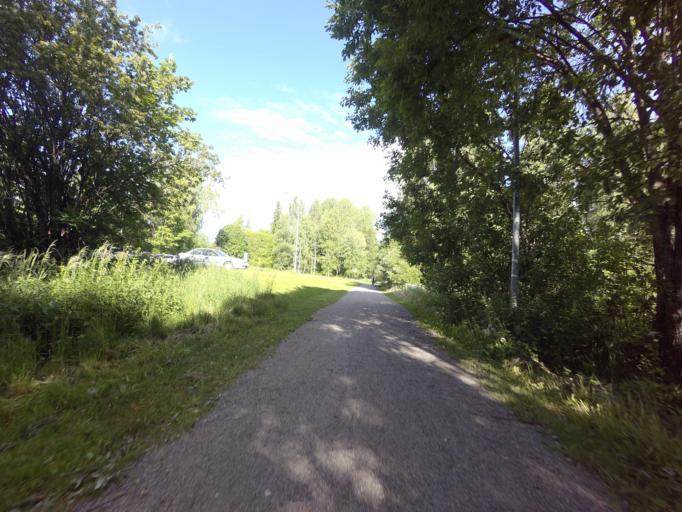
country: FI
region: Uusimaa
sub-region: Helsinki
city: Espoo
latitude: 60.1748
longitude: 24.6817
